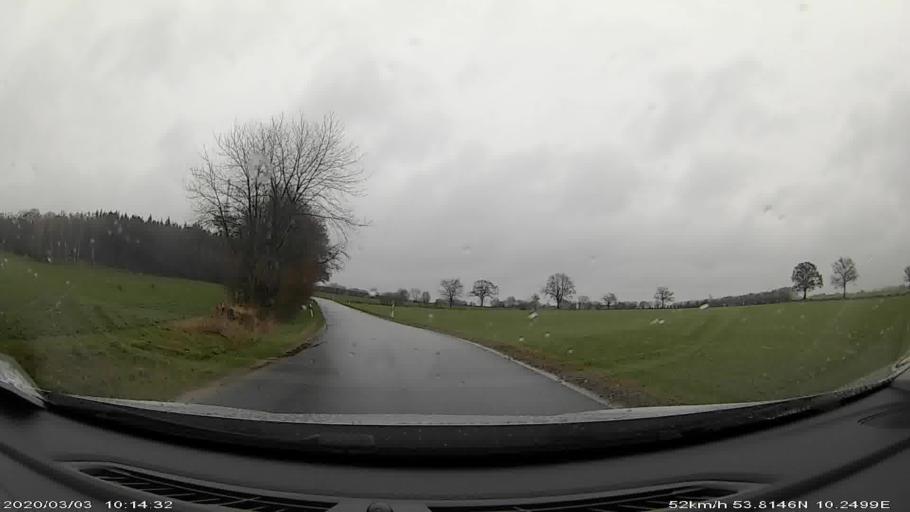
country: DE
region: Schleswig-Holstein
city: Sulfeld
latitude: 53.8175
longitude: 10.2532
